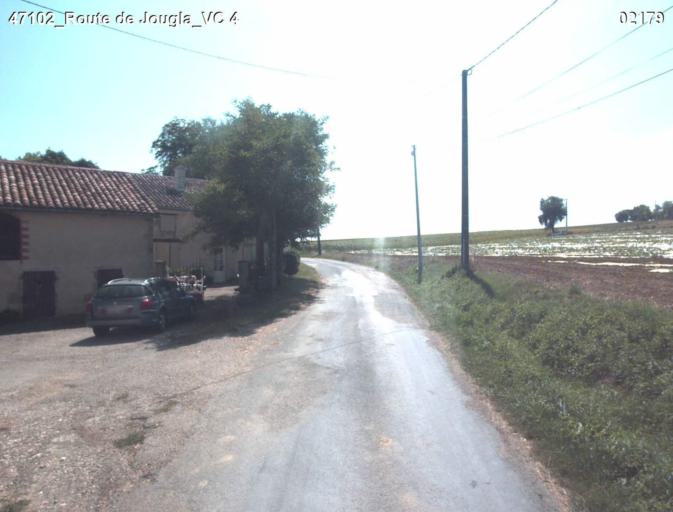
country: FR
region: Aquitaine
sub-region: Departement du Lot-et-Garonne
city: Nerac
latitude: 44.0594
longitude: 0.4304
